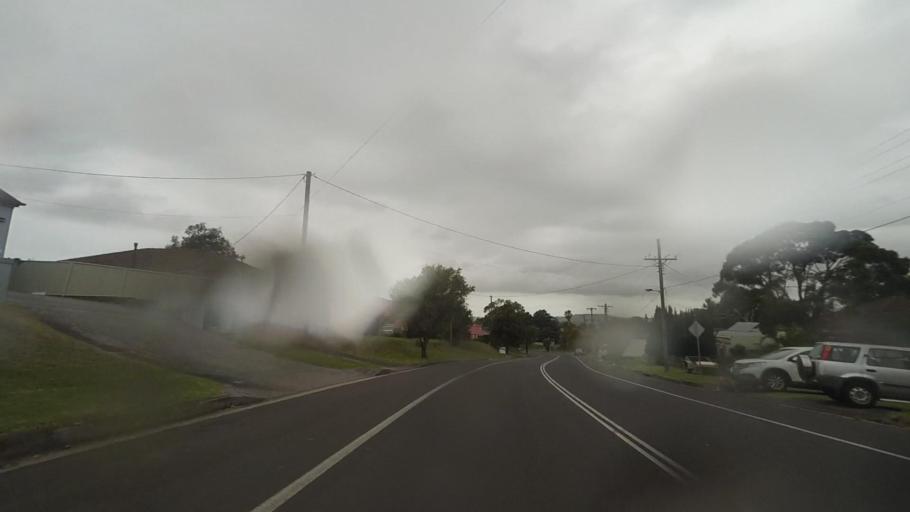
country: AU
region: New South Wales
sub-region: Wollongong
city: Mount Keira
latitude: -34.4166
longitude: 150.8598
